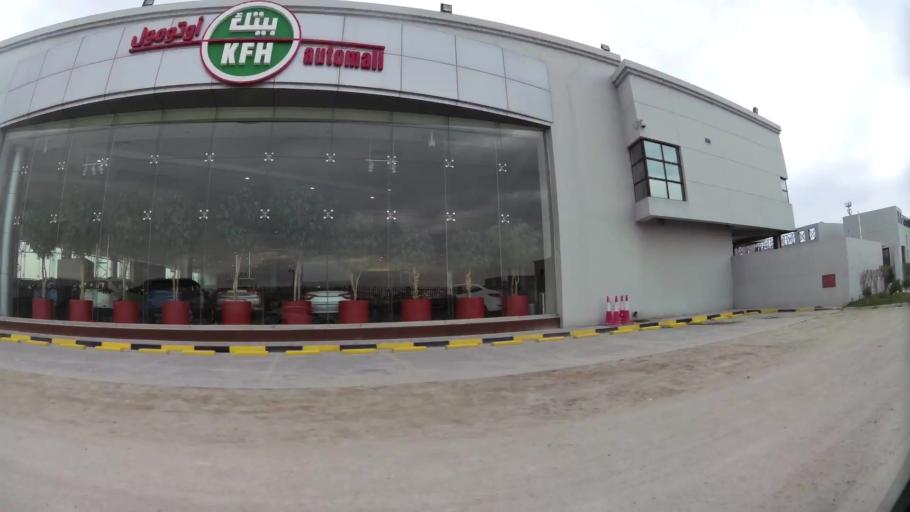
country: BH
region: Northern
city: Sitrah
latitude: 26.1683
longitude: 50.6049
